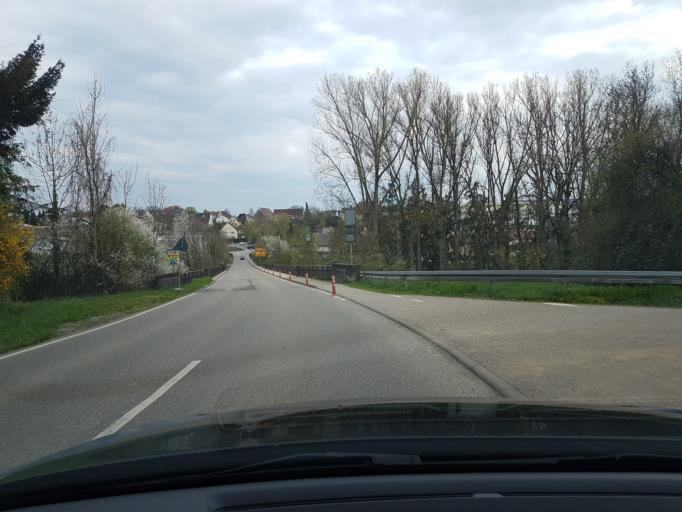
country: DE
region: Baden-Wuerttemberg
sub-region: Regierungsbezirk Stuttgart
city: Neuenstadt am Kocher
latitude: 49.2418
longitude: 9.3331
